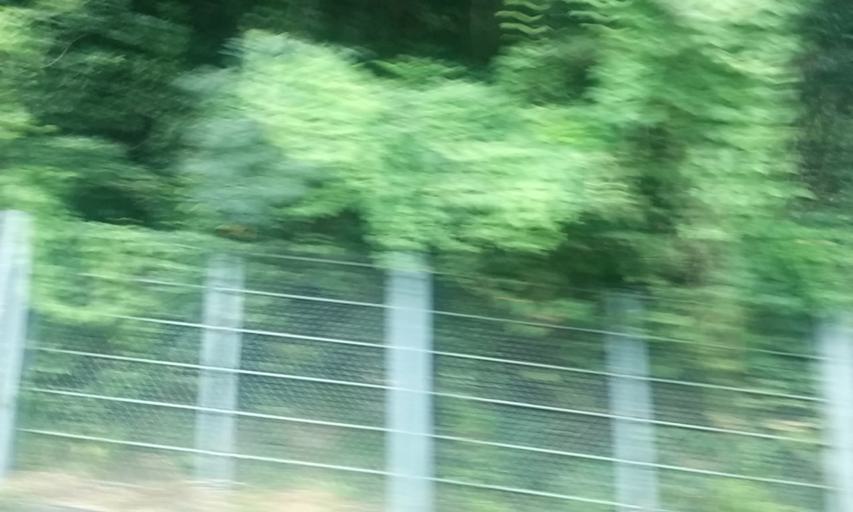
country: JP
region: Kyoto
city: Ayabe
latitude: 35.2080
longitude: 135.1995
